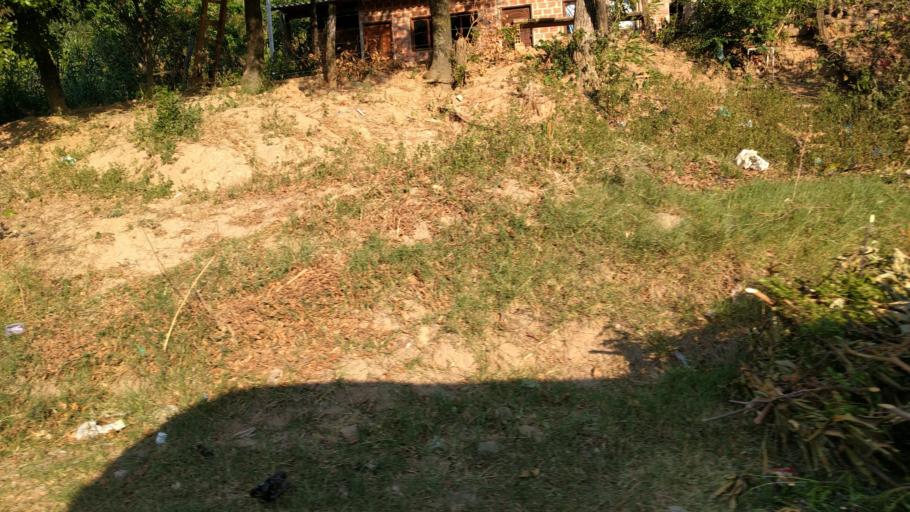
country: BO
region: Santa Cruz
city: Limoncito
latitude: -18.0268
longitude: -63.4016
